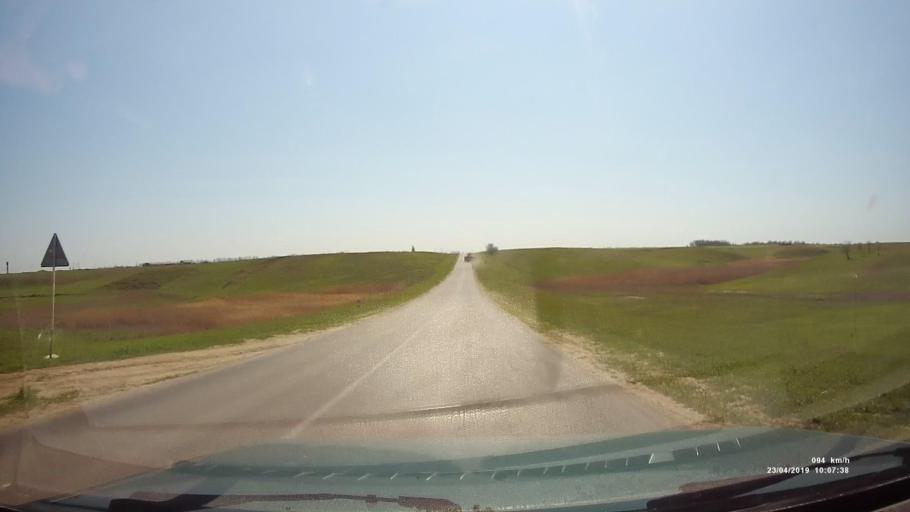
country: RU
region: Rostov
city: Sovetskoye
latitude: 46.7236
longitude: 42.2566
